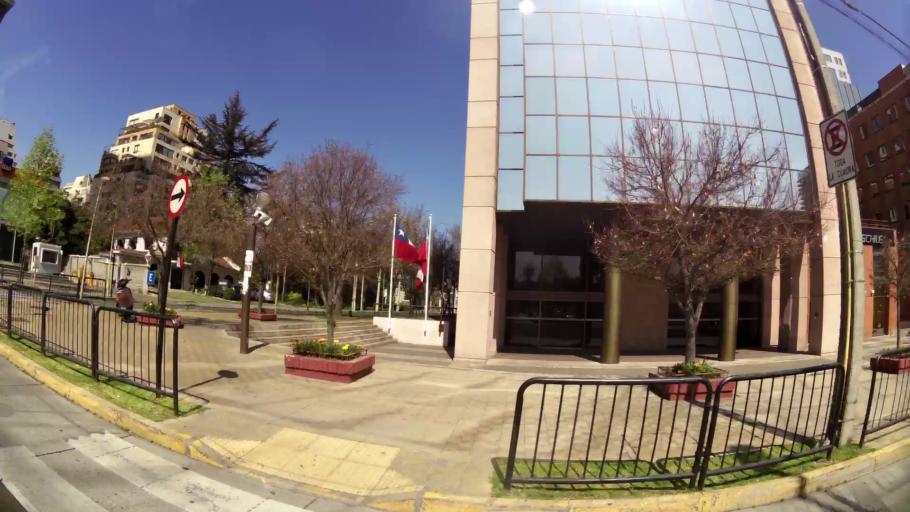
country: CL
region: Santiago Metropolitan
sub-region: Provincia de Santiago
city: Villa Presidente Frei, Nunoa, Santiago, Chile
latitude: -33.4144
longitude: -70.5834
